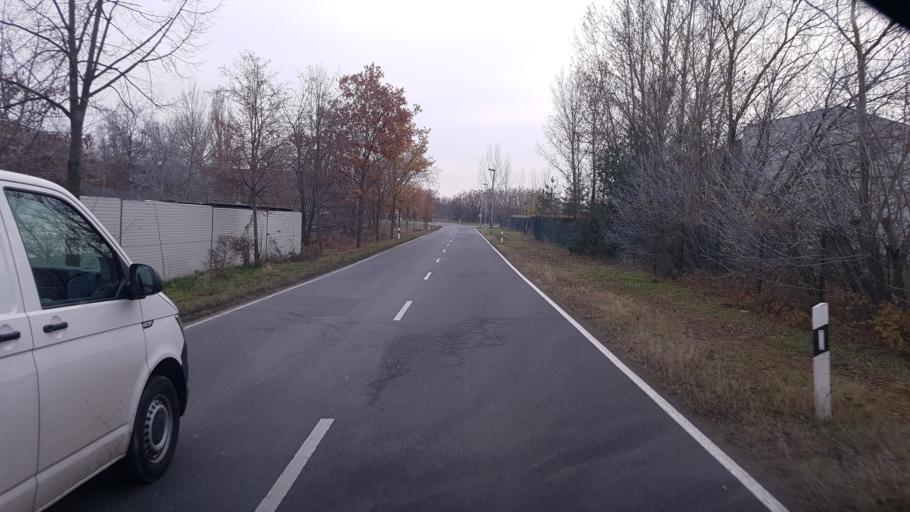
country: DE
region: Brandenburg
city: Eisenhuettenstadt
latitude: 52.1568
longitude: 14.6549
